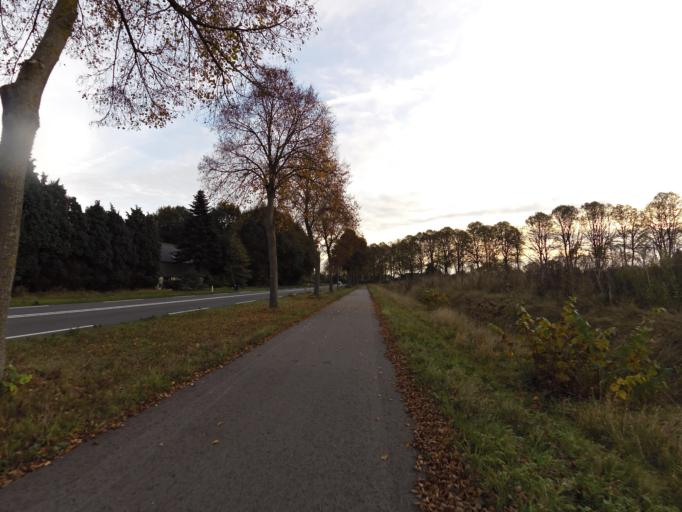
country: NL
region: Gelderland
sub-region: Gemeente Doetinchem
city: Doetinchem
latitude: 51.9535
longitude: 6.2187
